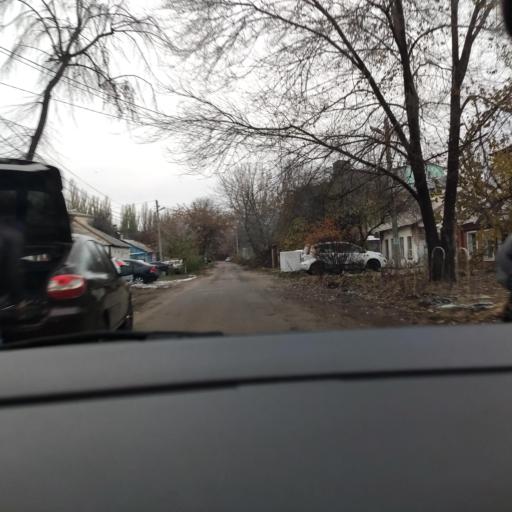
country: RU
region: Voronezj
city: Voronezh
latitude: 51.6743
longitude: 39.1978
